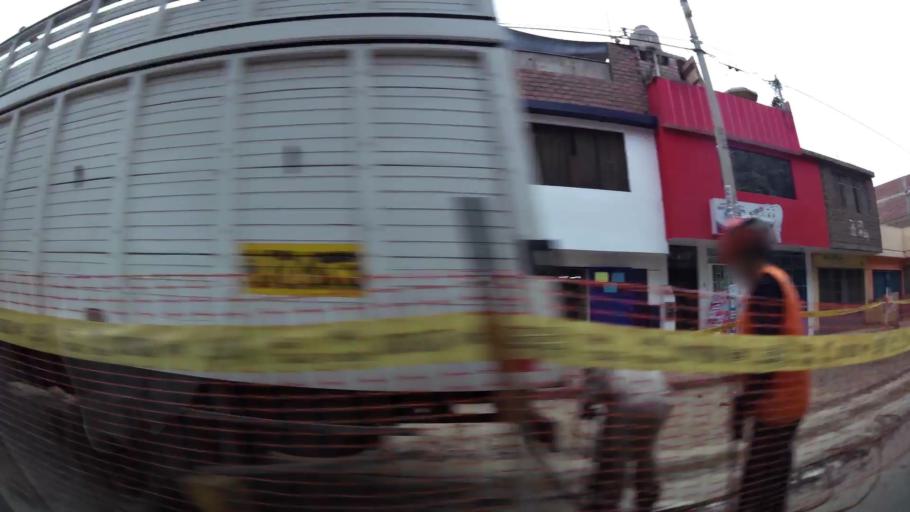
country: PE
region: Lima
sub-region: Lima
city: Urb. Santo Domingo
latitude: -11.9045
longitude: -77.0372
